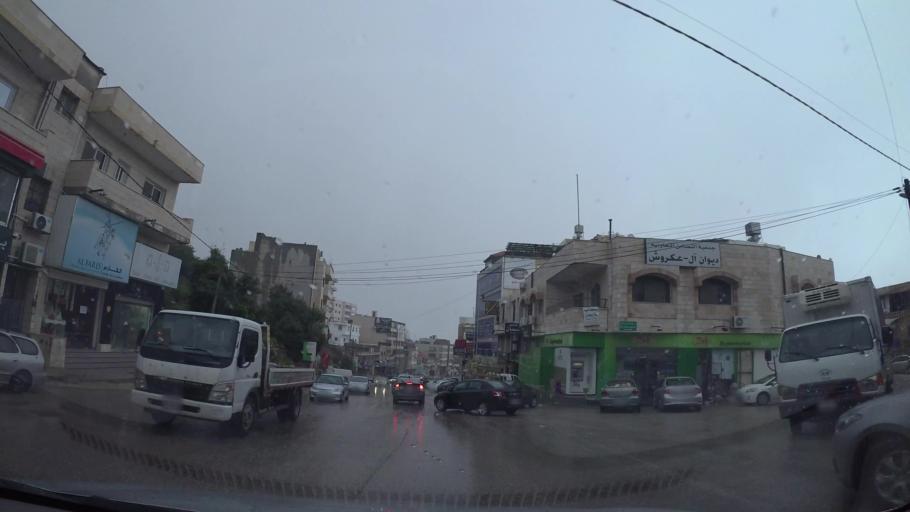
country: JO
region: Amman
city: Wadi as Sir
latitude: 32.0027
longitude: 35.7927
